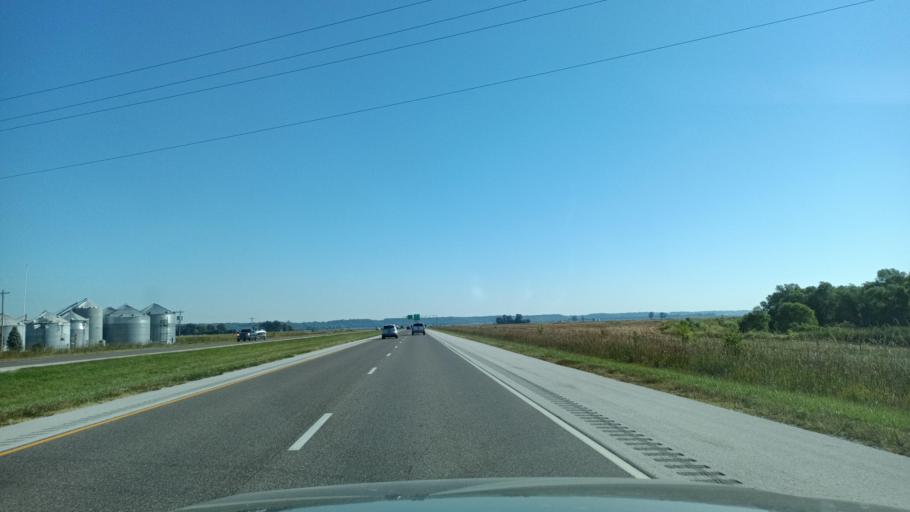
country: US
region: Missouri
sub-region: Marion County
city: Hannibal
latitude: 39.7350
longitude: -91.3140
